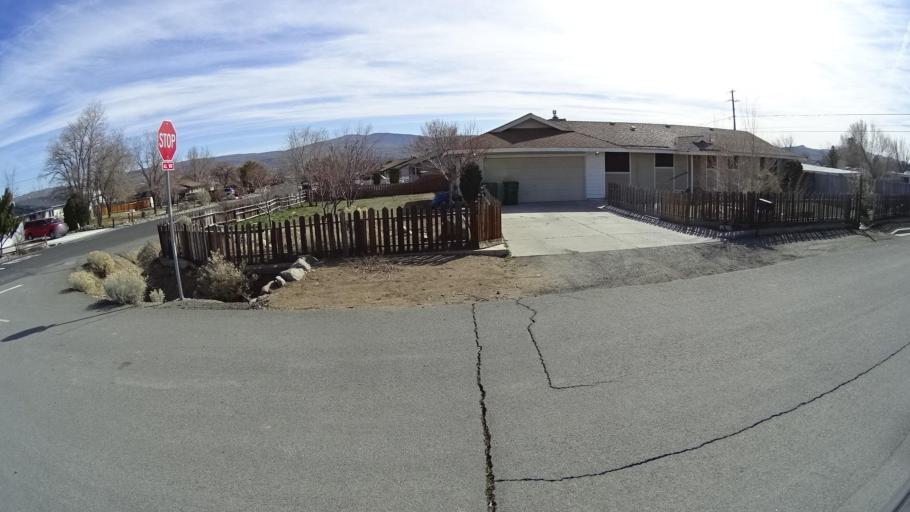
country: US
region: Nevada
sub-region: Washoe County
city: Spanish Springs
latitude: 39.6276
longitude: -119.7251
